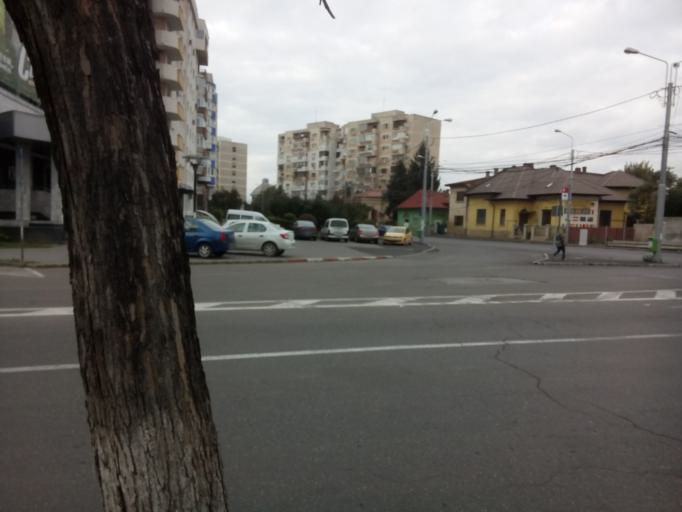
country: RO
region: Prahova
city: Ploiesti
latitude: 44.9420
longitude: 26.0280
